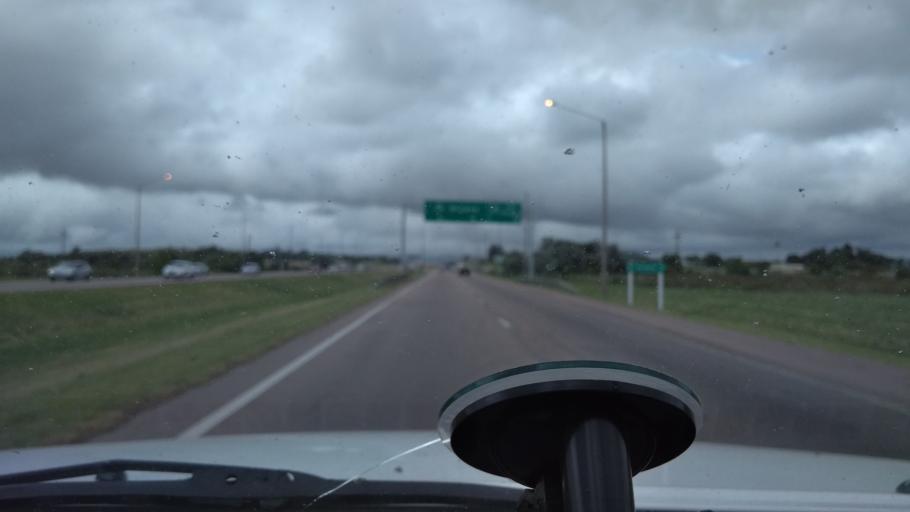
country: UY
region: Canelones
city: La Paz
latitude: -34.7770
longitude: -56.2723
